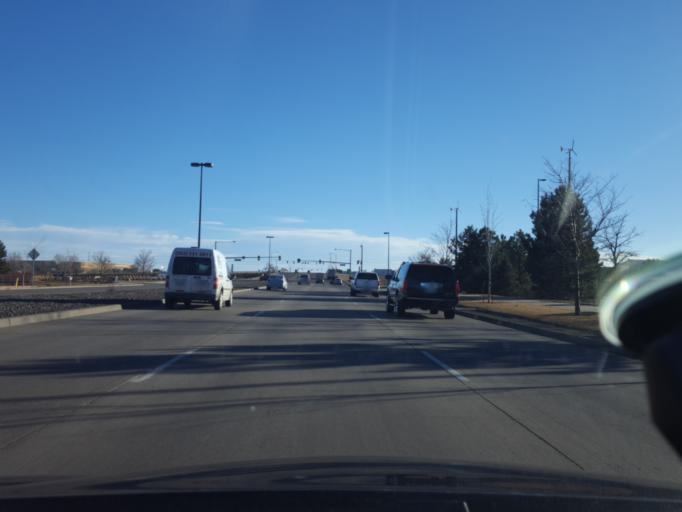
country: US
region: Colorado
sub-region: Adams County
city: Aurora
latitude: 39.7636
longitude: -104.7723
